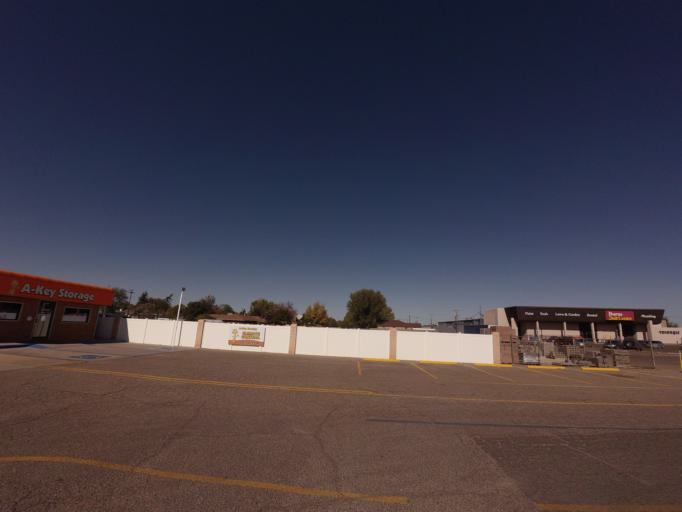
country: US
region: New Mexico
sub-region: Curry County
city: Clovis
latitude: 34.4213
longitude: -103.1978
